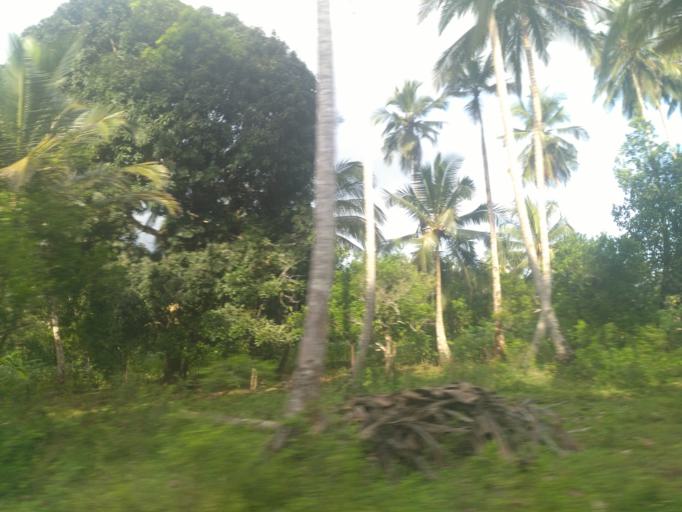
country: TZ
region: Zanzibar Central/South
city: Koani
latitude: -6.1050
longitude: 39.3024
